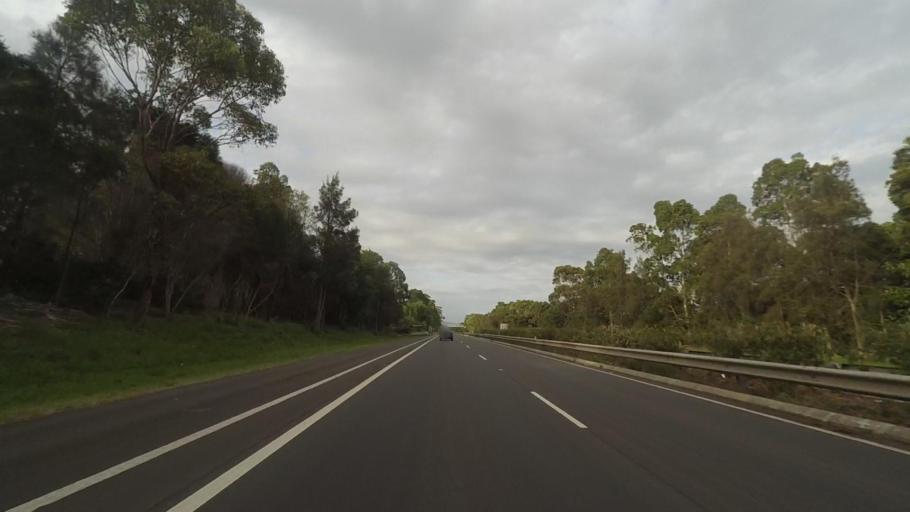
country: AU
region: New South Wales
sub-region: Wollongong
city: Fairy Meadow
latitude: -34.3993
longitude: 150.8939
